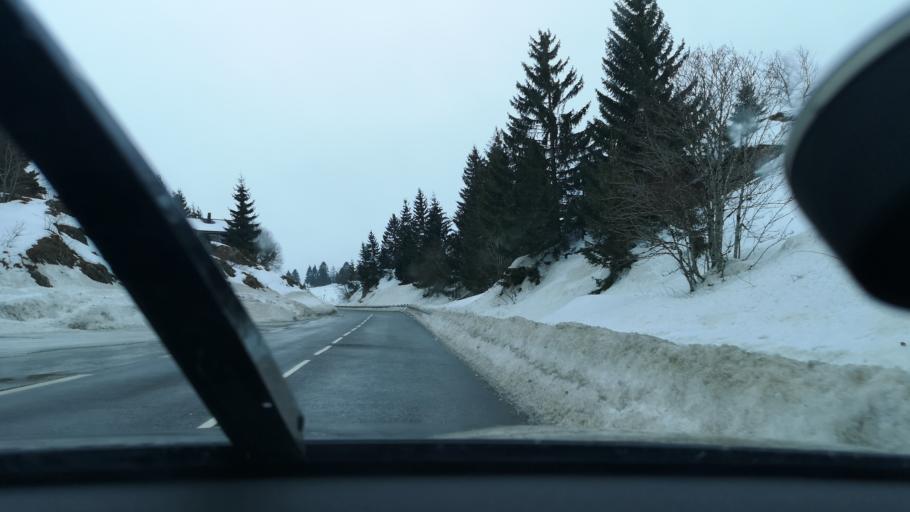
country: FR
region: Franche-Comte
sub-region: Departement du Doubs
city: Les Fourgs
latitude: 46.8345
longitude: 6.4160
